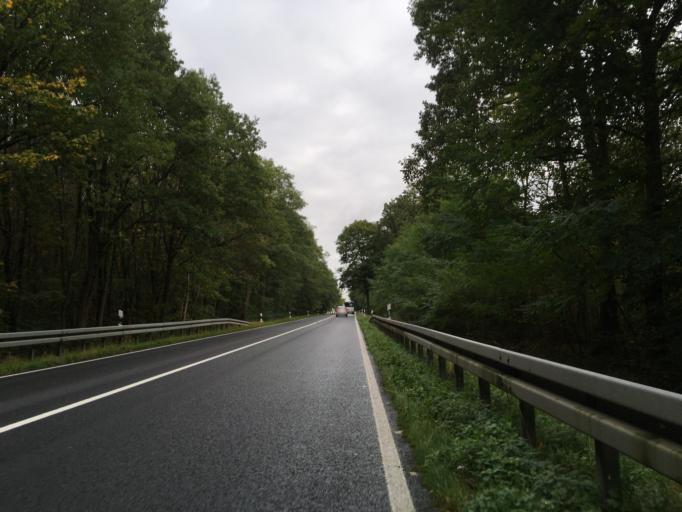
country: DE
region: Brandenburg
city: Werftpfuhl
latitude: 52.6896
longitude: 13.8589
